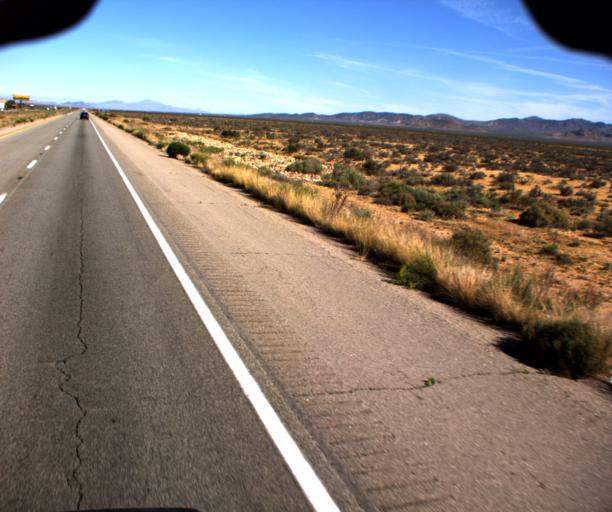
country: US
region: Arizona
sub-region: Mohave County
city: Dolan Springs
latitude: 35.5555
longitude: -114.3701
